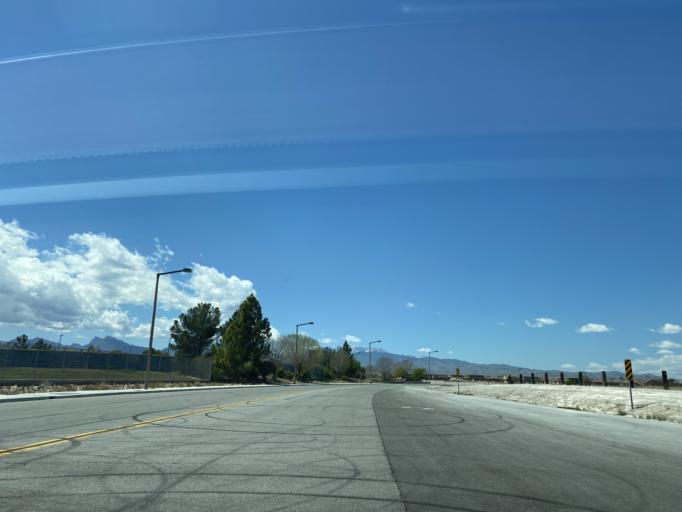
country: US
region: Nevada
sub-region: Clark County
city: North Las Vegas
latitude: 36.3206
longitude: -115.2093
